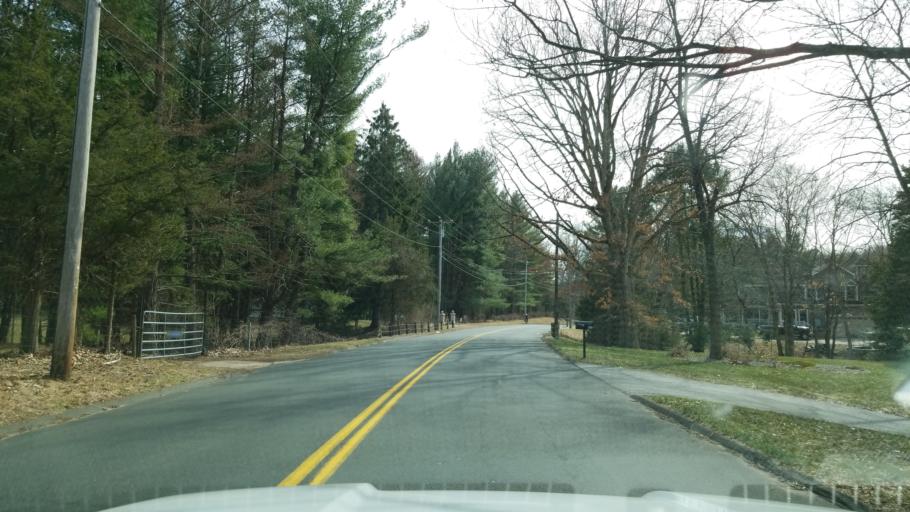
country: US
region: Connecticut
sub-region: Hartford County
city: Glastonbury Center
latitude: 41.6780
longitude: -72.5634
